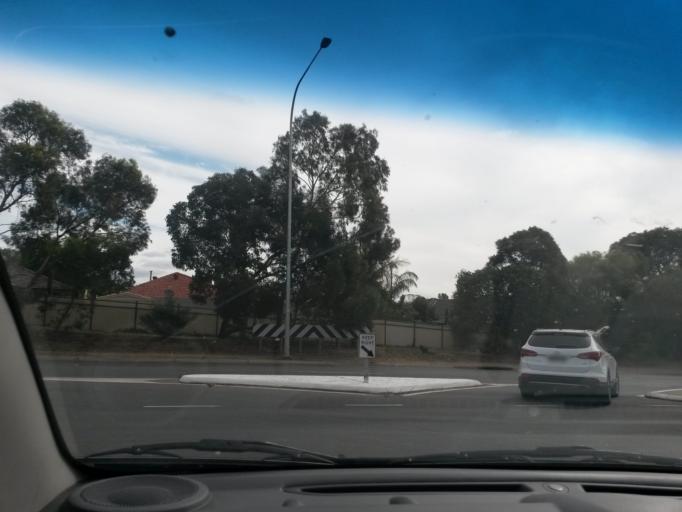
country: AU
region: South Australia
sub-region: Salisbury
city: Salisbury
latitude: -34.7698
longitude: 138.6787
